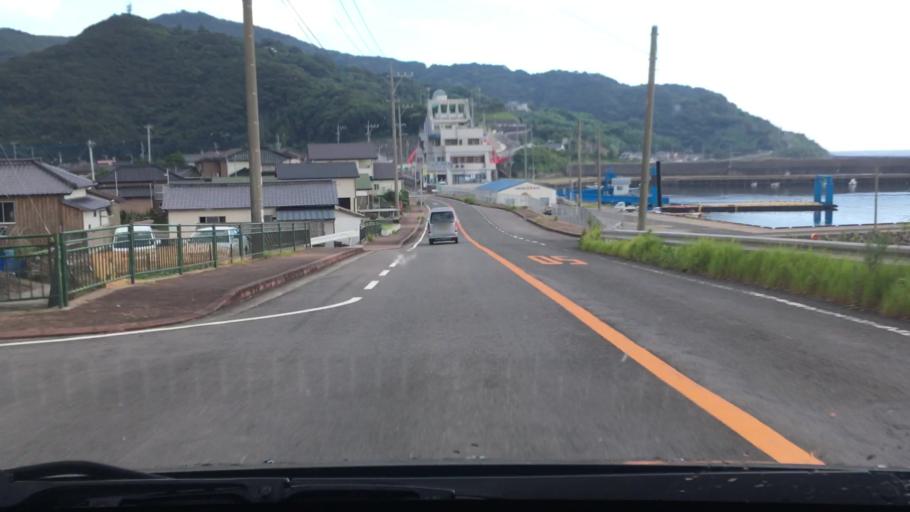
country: JP
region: Nagasaki
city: Togitsu
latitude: 32.8823
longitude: 129.6791
